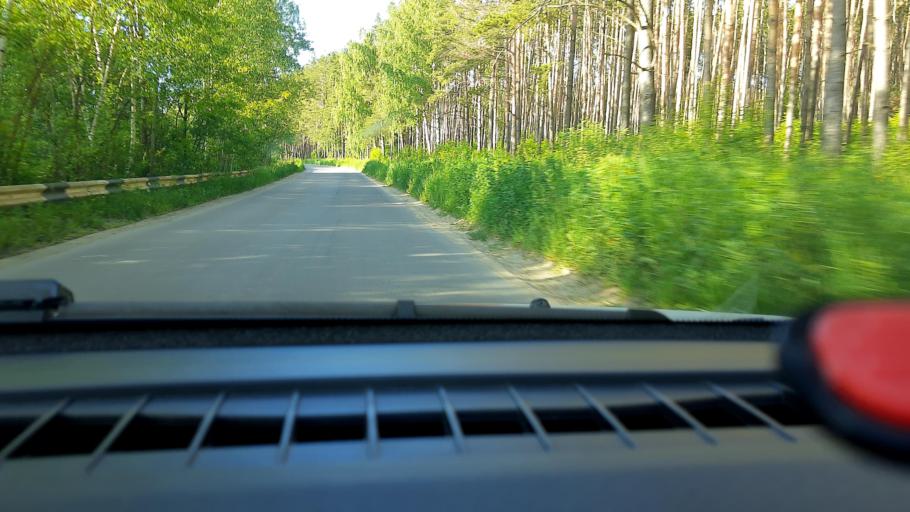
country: RU
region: Nizjnij Novgorod
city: Gorbatovka
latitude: 56.2267
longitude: 43.7615
